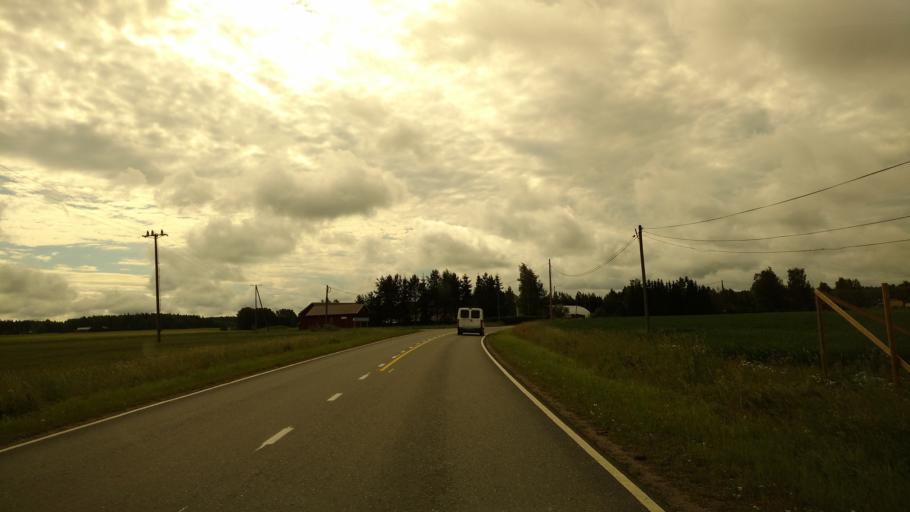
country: FI
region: Varsinais-Suomi
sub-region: Salo
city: Kuusjoki
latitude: 60.5404
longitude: 23.1662
